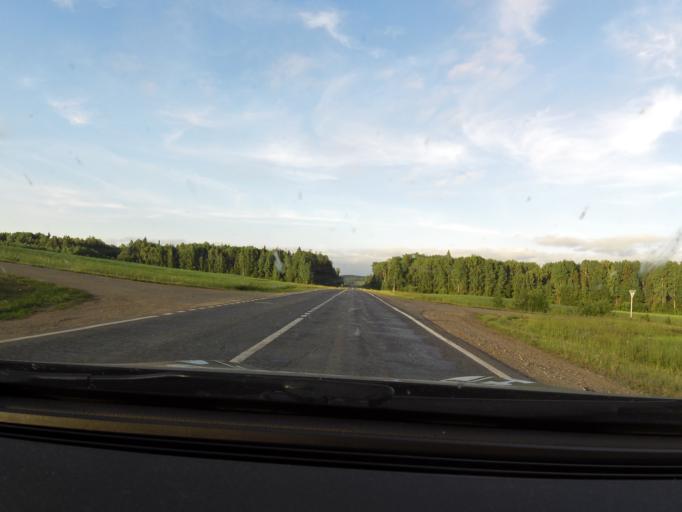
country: RU
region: Perm
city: Siva
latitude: 58.4864
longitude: 54.1543
